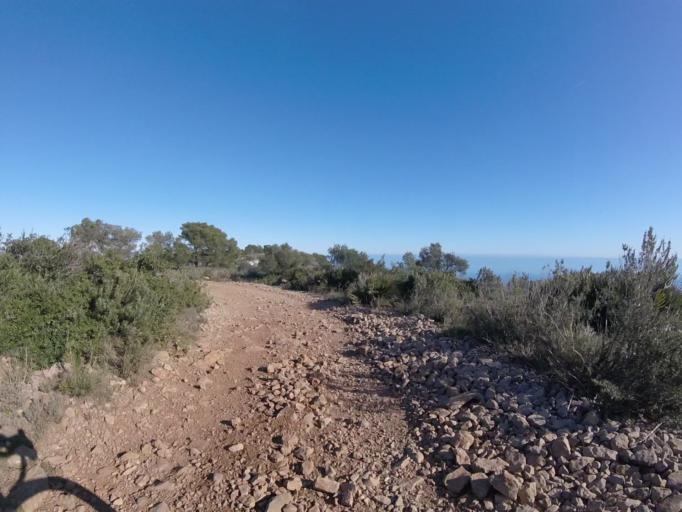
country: ES
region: Valencia
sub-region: Provincia de Castello
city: Orpesa/Oropesa del Mar
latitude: 40.0985
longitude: 0.1102
